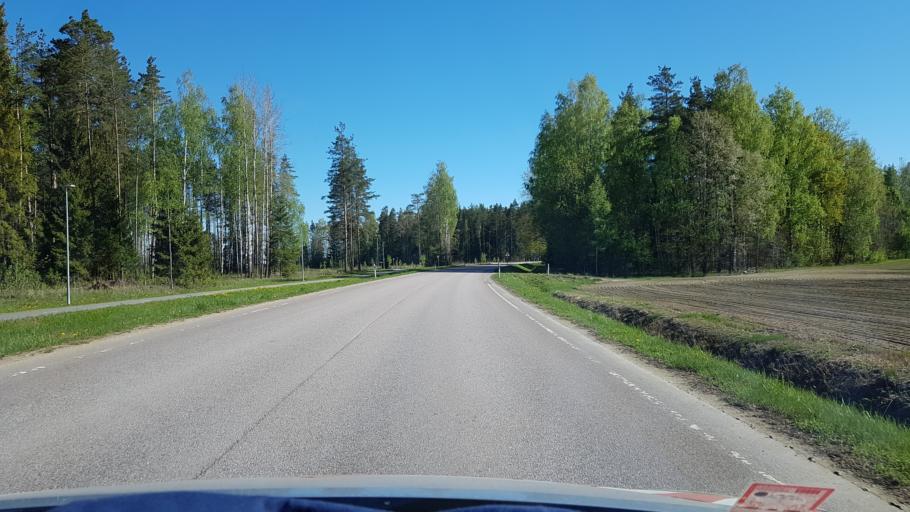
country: EE
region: Polvamaa
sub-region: Polva linn
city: Polva
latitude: 58.0953
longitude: 27.0939
